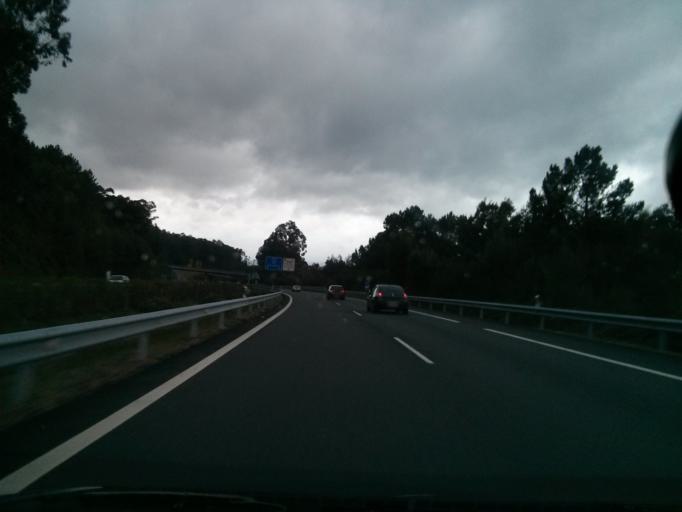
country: ES
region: Galicia
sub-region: Provincia de Pontevedra
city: Ponteareas
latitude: 42.1529
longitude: -8.4220
